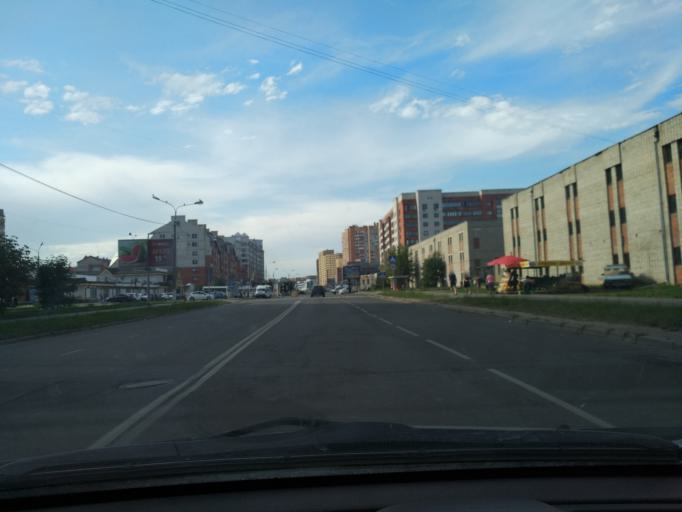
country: RU
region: Moskovskaya
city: Bykovo
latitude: 55.5976
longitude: 38.0910
